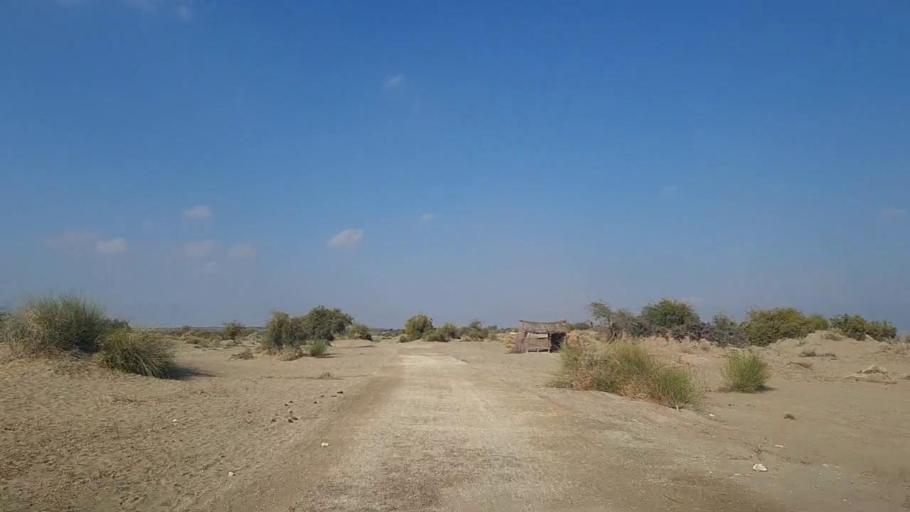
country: PK
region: Sindh
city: Tando Mittha Khan
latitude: 26.0239
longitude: 69.2513
